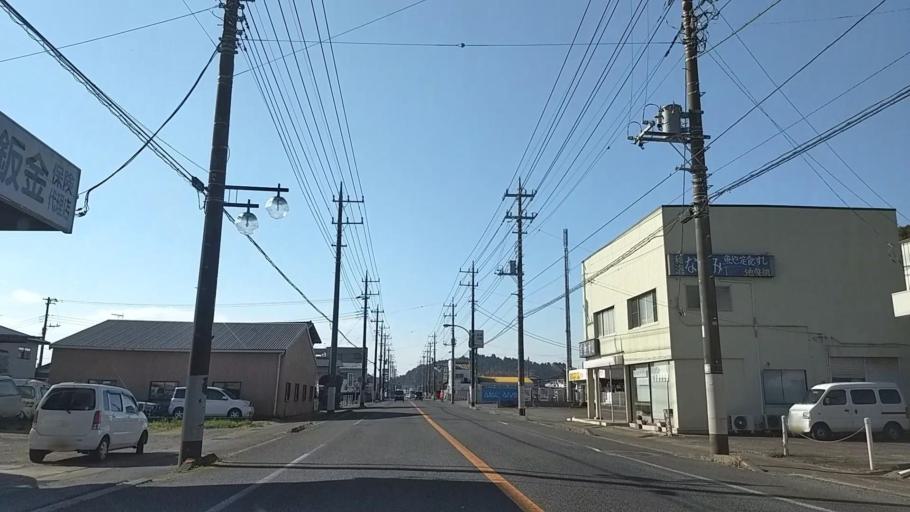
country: JP
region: Chiba
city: Yokaichiba
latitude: 35.6930
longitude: 140.5336
